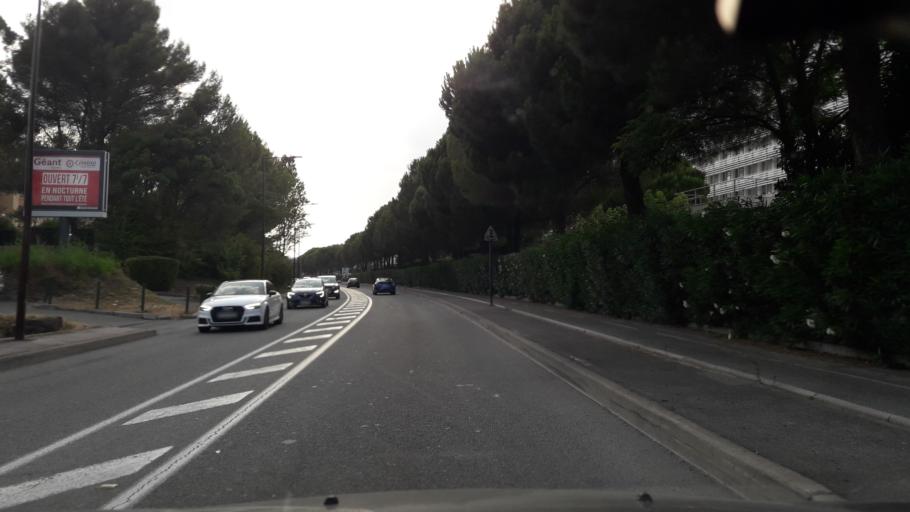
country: FR
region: Provence-Alpes-Cote d'Azur
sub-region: Departement du Var
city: Frejus
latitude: 43.4380
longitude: 6.7533
